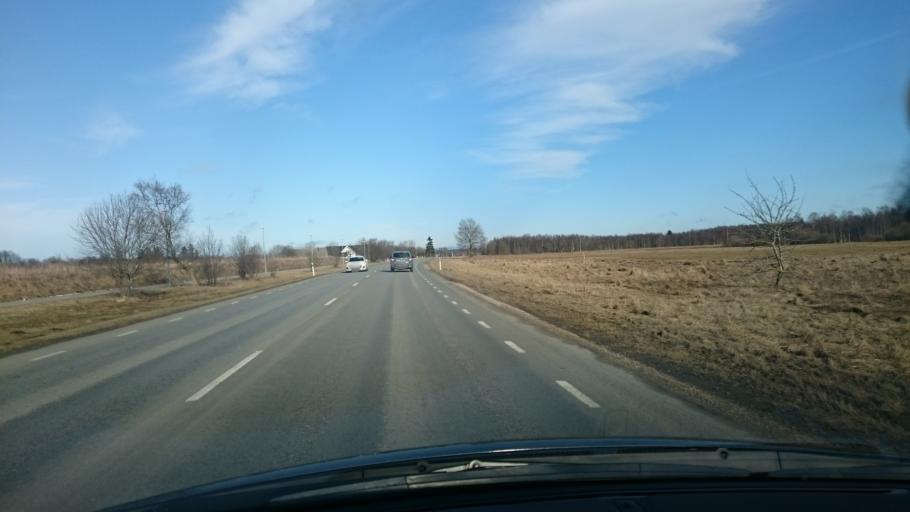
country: EE
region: Harju
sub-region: Keila linn
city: Keila
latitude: 59.4470
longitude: 24.3828
